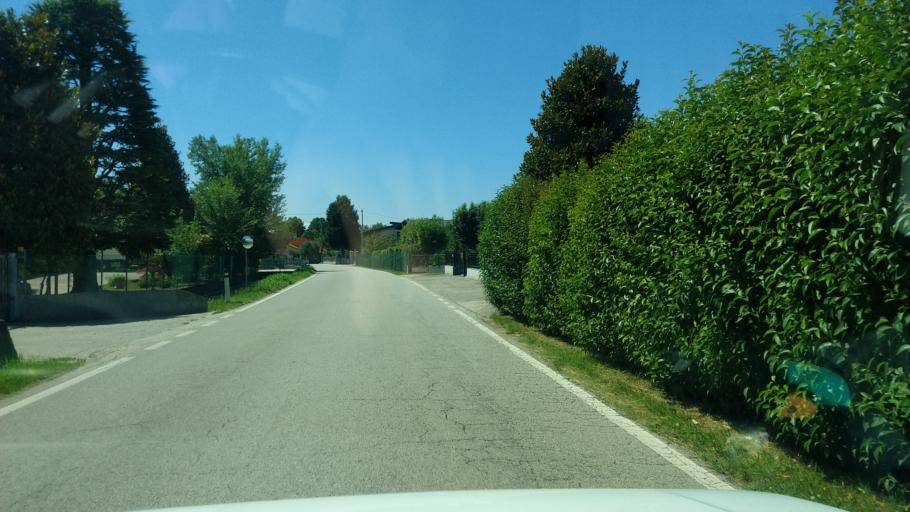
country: IT
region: Veneto
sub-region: Provincia di Vicenza
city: Preara-Moraro-Leva Nord
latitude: 45.6881
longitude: 11.5399
